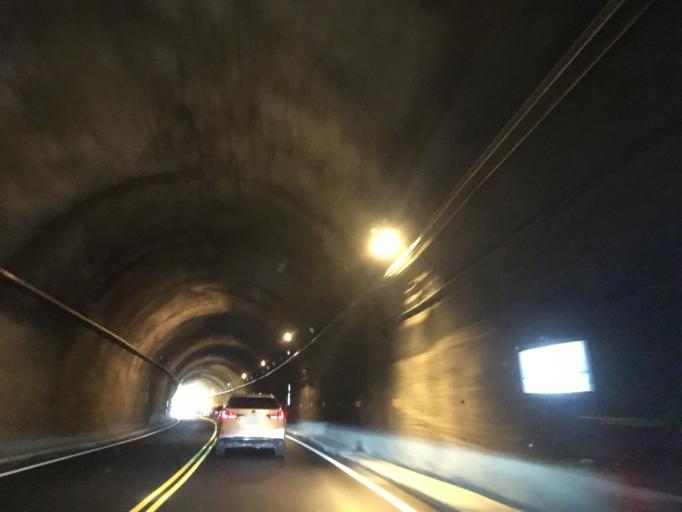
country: TW
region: Taiwan
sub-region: Hualien
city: Hualian
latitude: 24.1723
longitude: 121.5734
